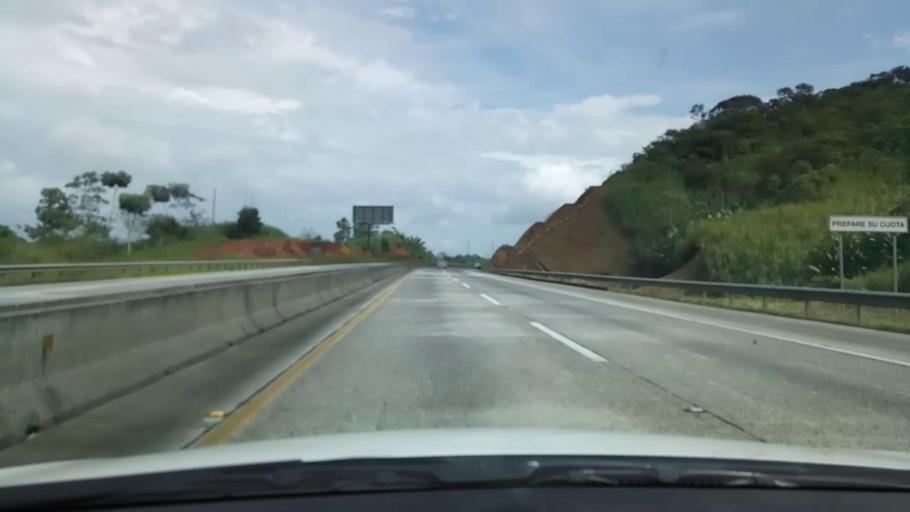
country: PA
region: Colon
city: Buena Vista
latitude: 9.2726
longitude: -79.7113
